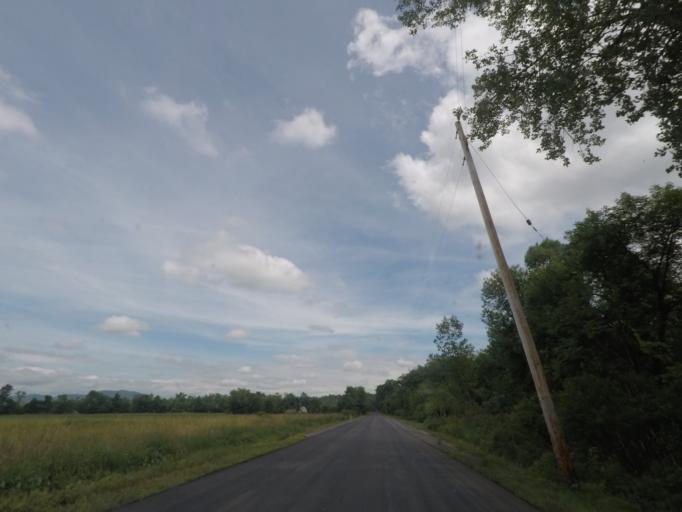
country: US
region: New York
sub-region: Saratoga County
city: Stillwater
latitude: 42.9905
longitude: -73.6147
